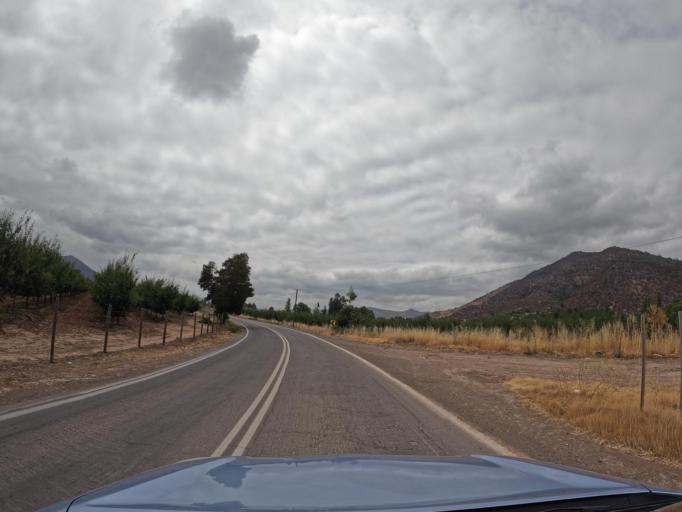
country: CL
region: Maule
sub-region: Provincia de Curico
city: Teno
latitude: -34.7574
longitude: -71.2162
